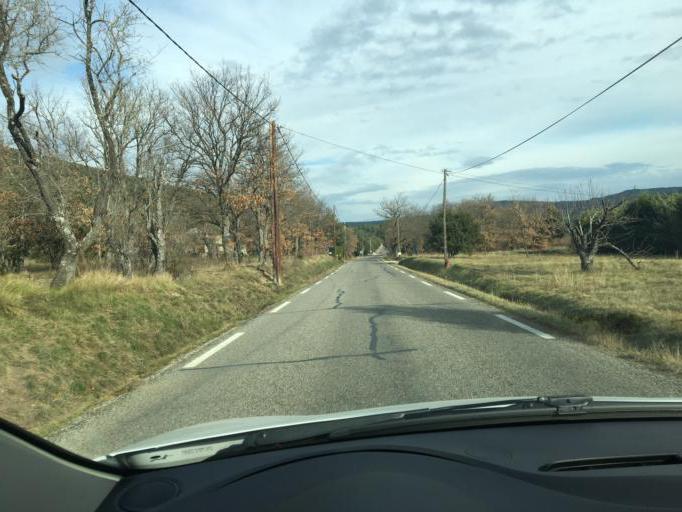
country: FR
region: Provence-Alpes-Cote d'Azur
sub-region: Departement du Vaucluse
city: Saignon
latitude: 43.9202
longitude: 5.4944
